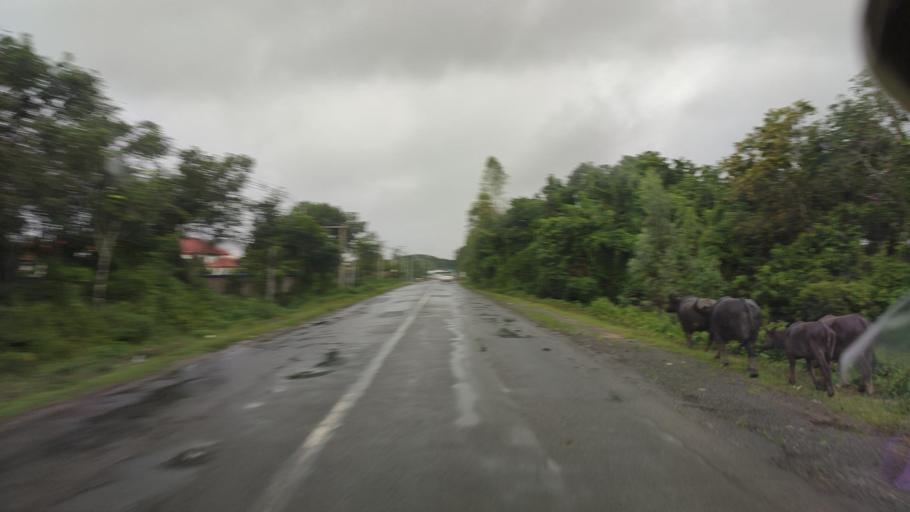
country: MM
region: Bago
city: Bago
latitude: 17.3626
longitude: 96.4571
